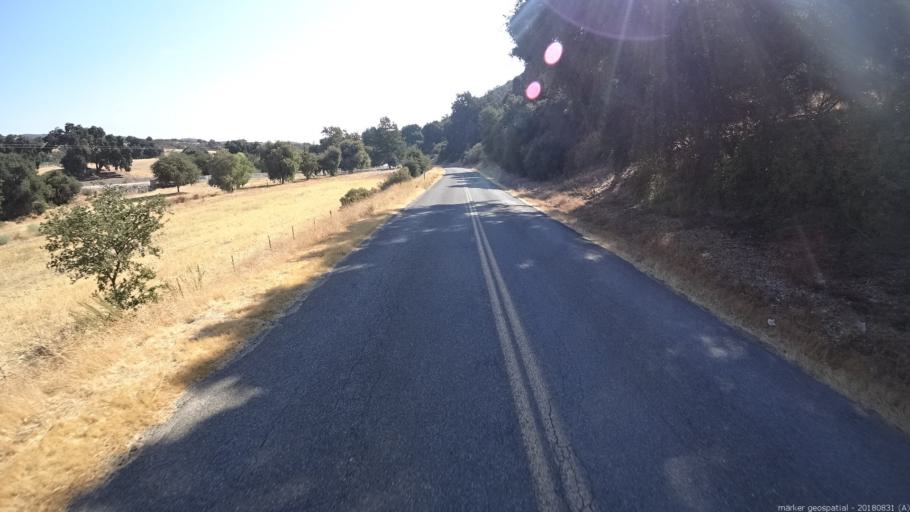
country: US
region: California
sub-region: Monterey County
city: King City
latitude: 36.1503
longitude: -121.1910
